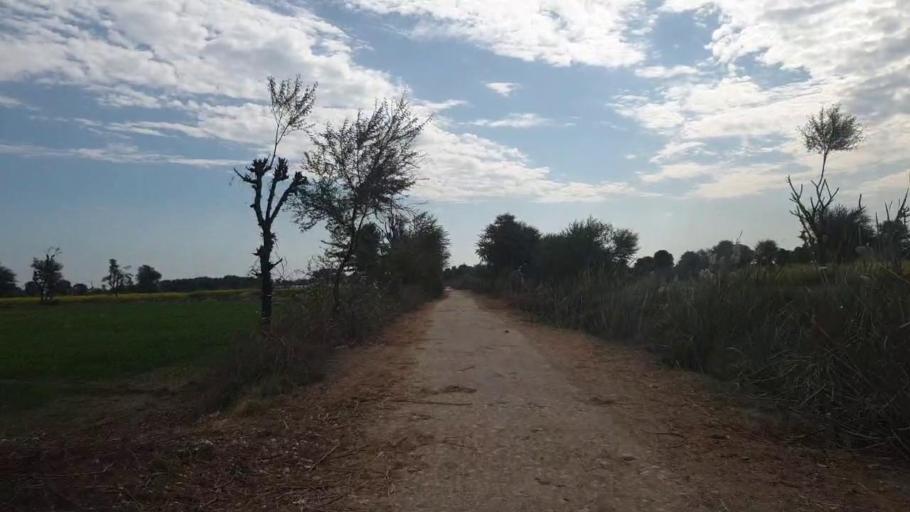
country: PK
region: Sindh
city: Jhol
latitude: 25.9886
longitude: 68.8994
